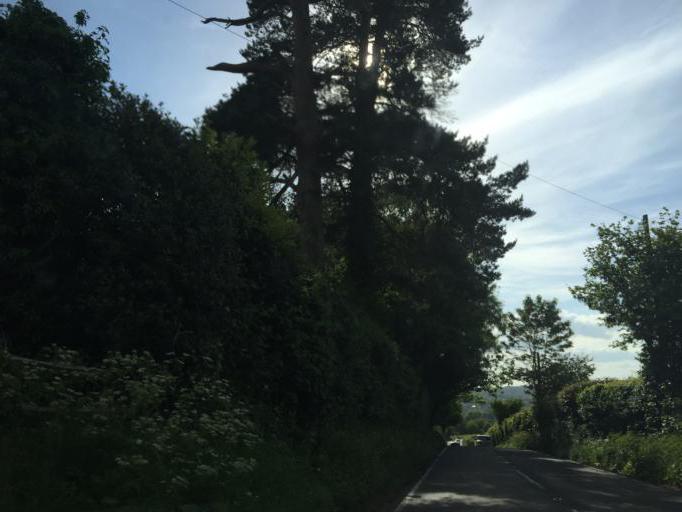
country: GB
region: England
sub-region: East Sussex
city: Crowborough
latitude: 51.0464
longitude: 0.2085
